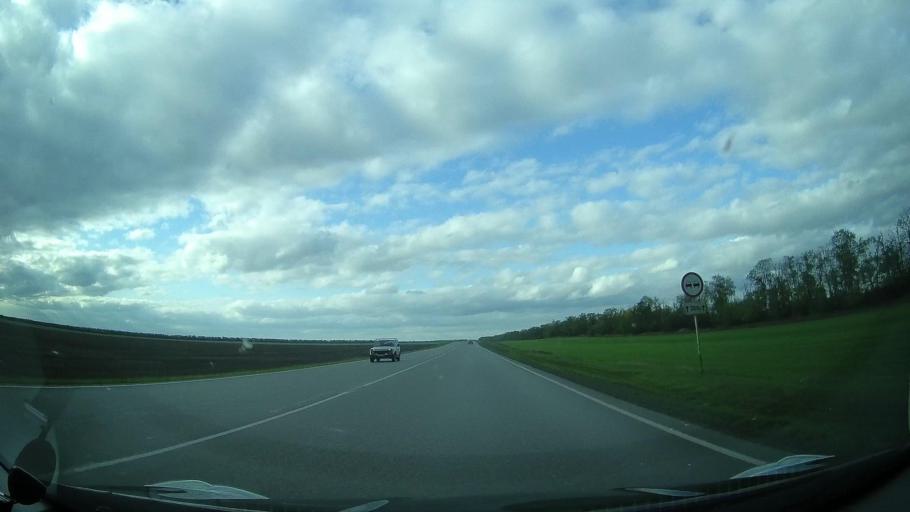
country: RU
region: Rostov
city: Kagal'nitskaya
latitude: 46.9000
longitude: 40.1236
